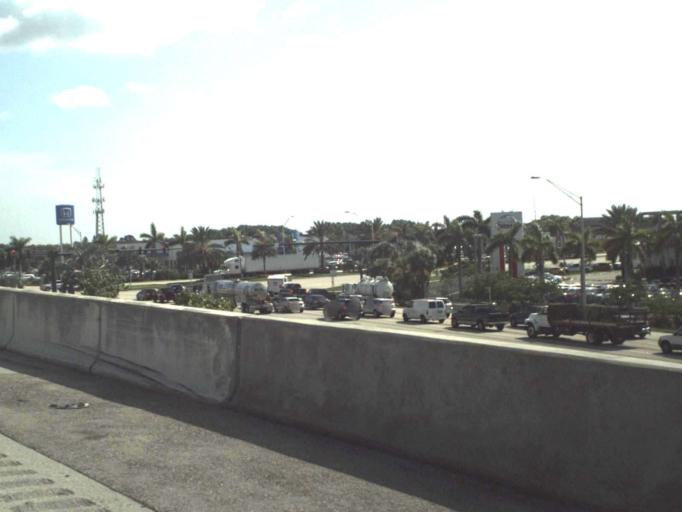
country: US
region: Florida
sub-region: Palm Beach County
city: Mangonia Park
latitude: 26.7819
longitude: -80.0989
